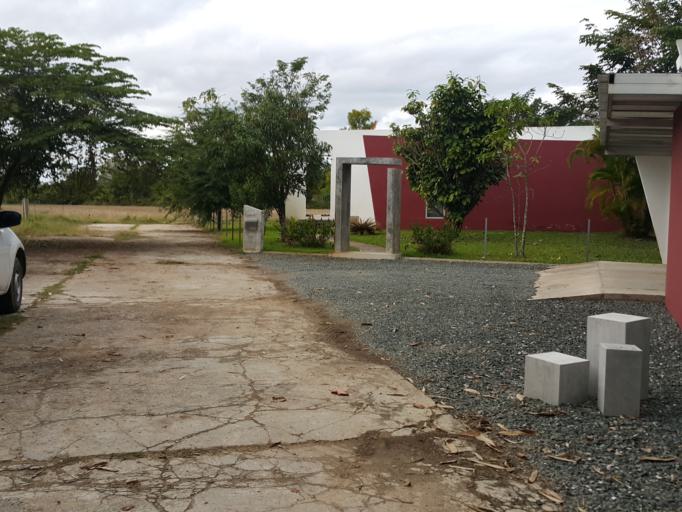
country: TH
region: Chiang Mai
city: San Sai
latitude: 18.8659
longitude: 99.1008
